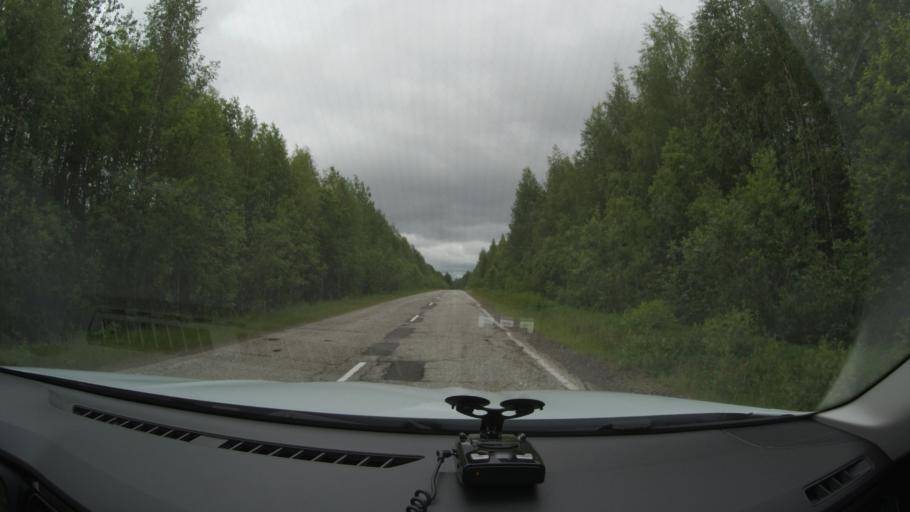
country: RU
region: Komi Republic
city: Nizhniy Odes
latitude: 63.6049
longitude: 54.5164
